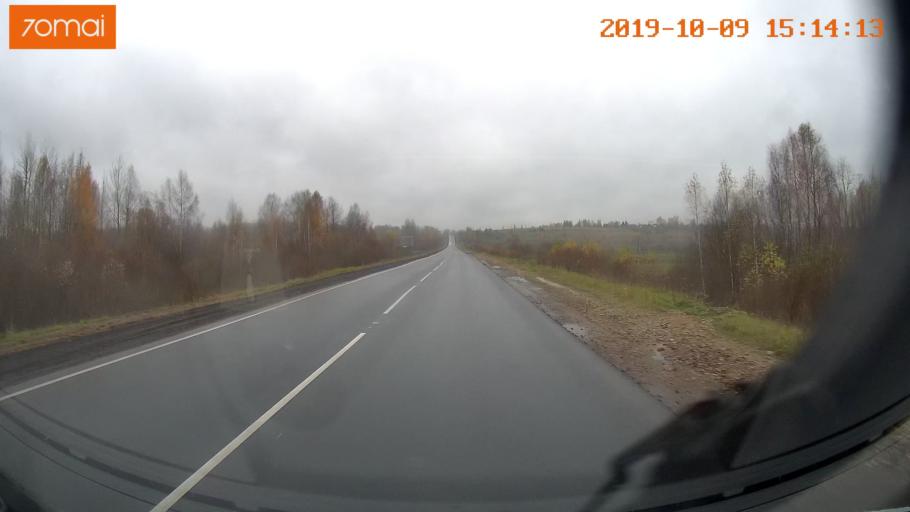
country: RU
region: Kostroma
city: Susanino
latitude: 58.1371
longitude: 41.6041
